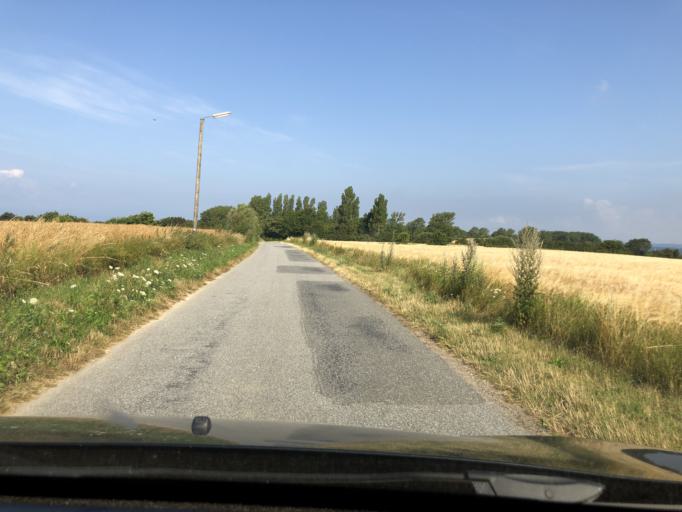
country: DK
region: South Denmark
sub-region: Faaborg-Midtfyn Kommune
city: Faaborg
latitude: 54.9500
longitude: 10.2314
